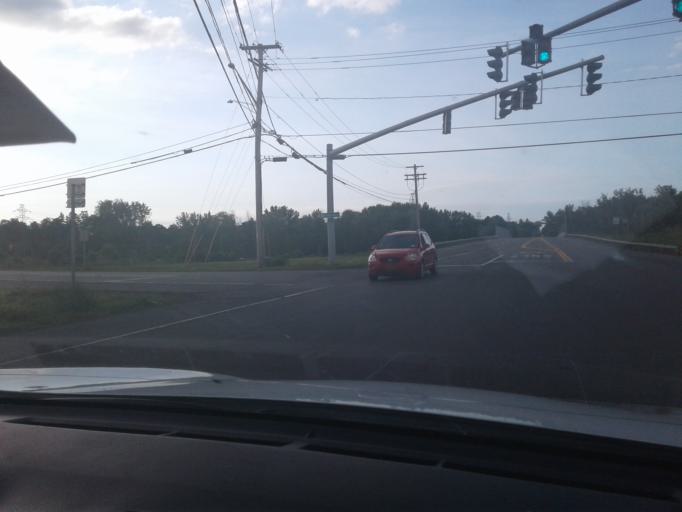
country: US
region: New York
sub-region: Onondaga County
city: East Syracuse
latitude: 43.0928
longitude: -76.0593
